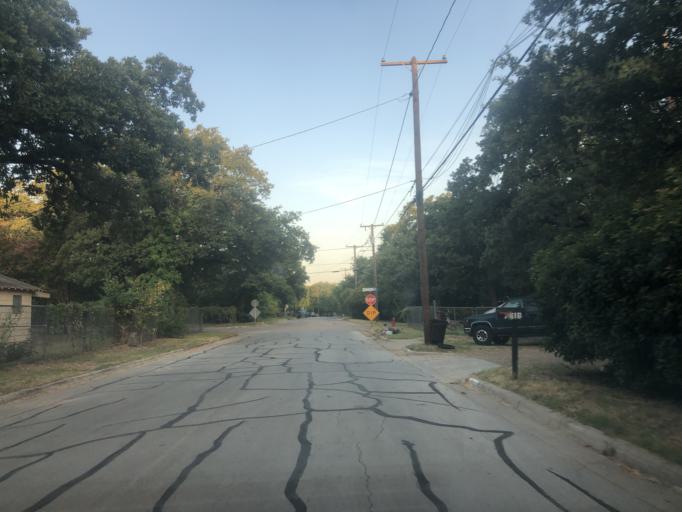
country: US
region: Texas
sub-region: Tarrant County
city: Lake Worth
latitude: 32.8050
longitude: -97.4490
